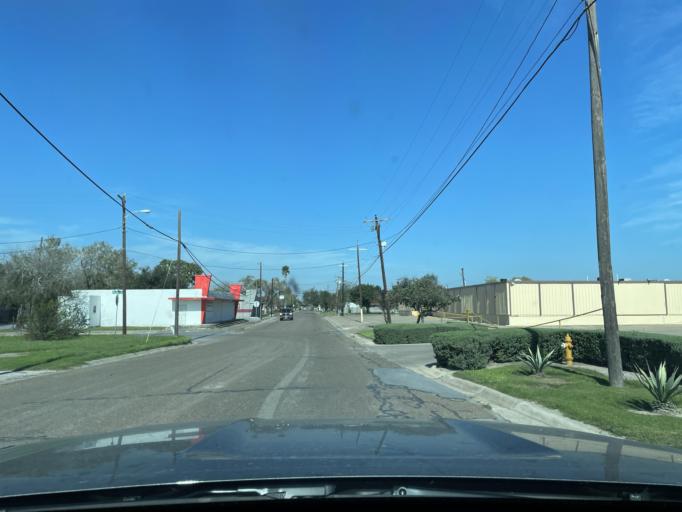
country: US
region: Texas
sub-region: Cameron County
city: Harlingen
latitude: 26.1928
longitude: -97.7092
